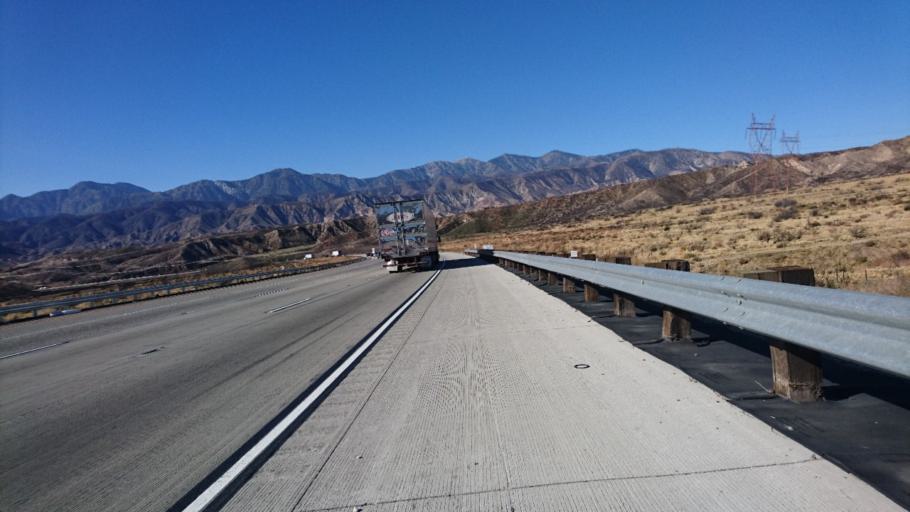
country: US
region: California
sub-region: San Bernardino County
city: Oak Hills
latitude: 34.3474
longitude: -117.4763
